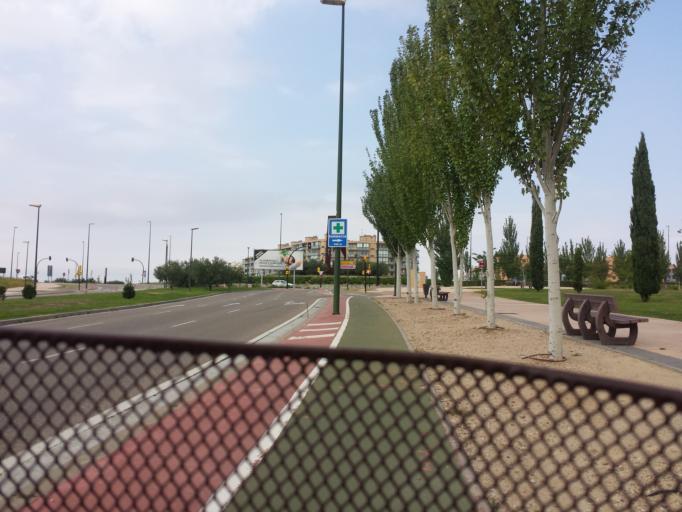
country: ES
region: Aragon
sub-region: Provincia de Zaragoza
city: Montecanal
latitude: 41.6194
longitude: -0.9253
